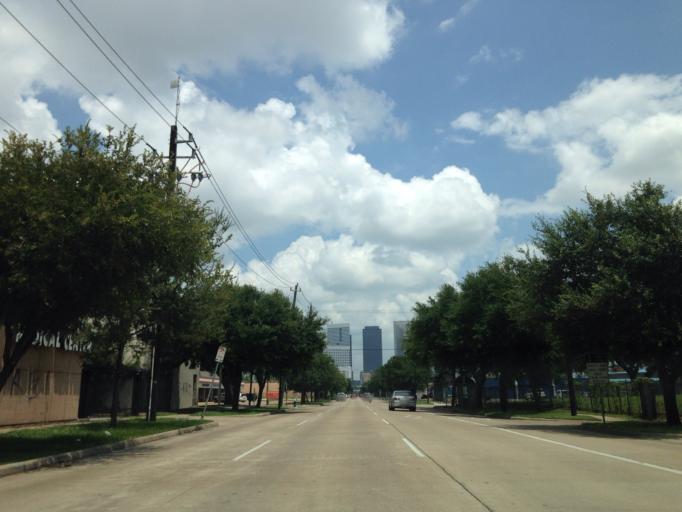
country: US
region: Texas
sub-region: Harris County
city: Houston
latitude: 29.7418
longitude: -95.3744
